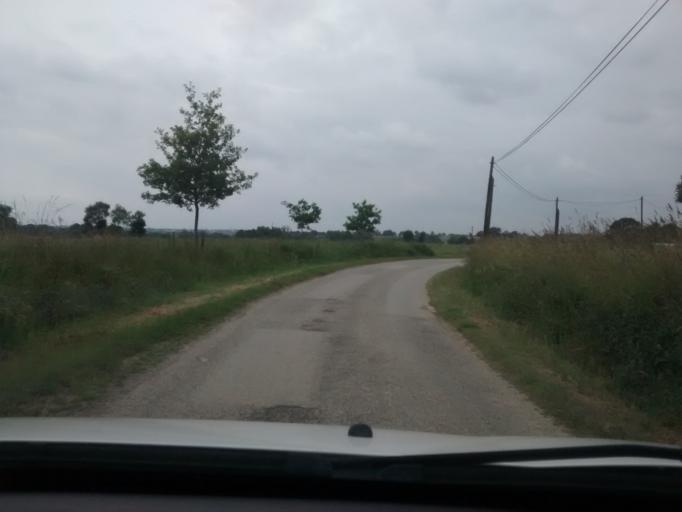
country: FR
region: Brittany
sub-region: Departement d'Ille-et-Vilaine
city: Servon-sur-Vilaine
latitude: 48.1416
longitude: -1.4750
